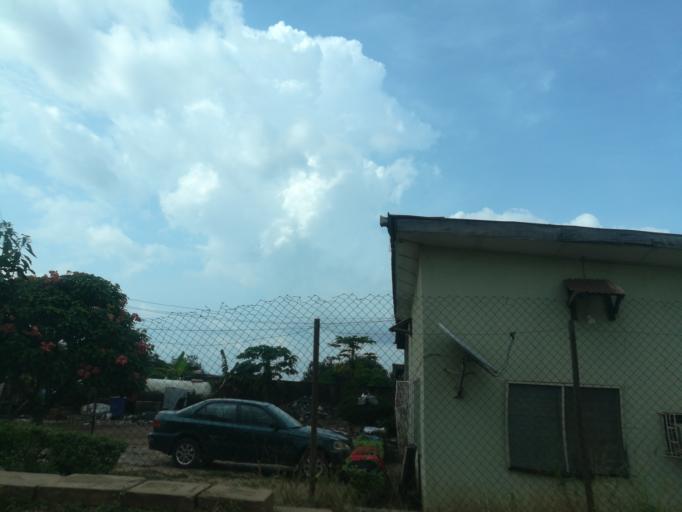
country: NG
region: Oyo
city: Ibadan
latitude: 7.4520
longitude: 3.9026
